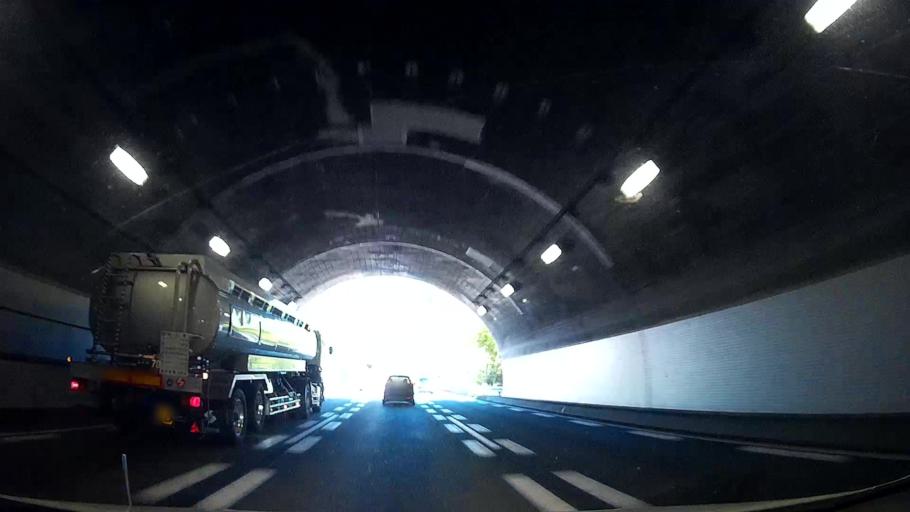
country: JP
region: Shizuoka
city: Gotemba
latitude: 35.3511
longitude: 139.0023
